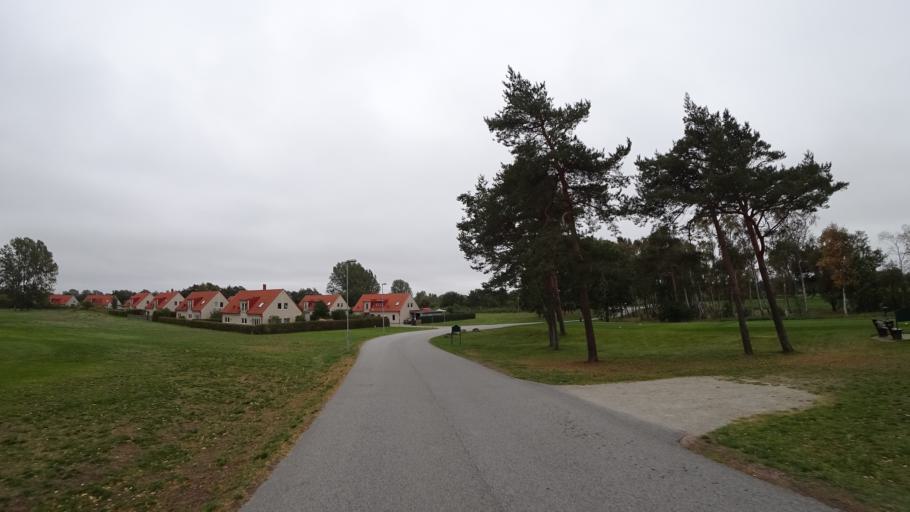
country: SE
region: Skane
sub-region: Kavlinge Kommun
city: Hofterup
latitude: 55.7891
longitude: 12.9465
